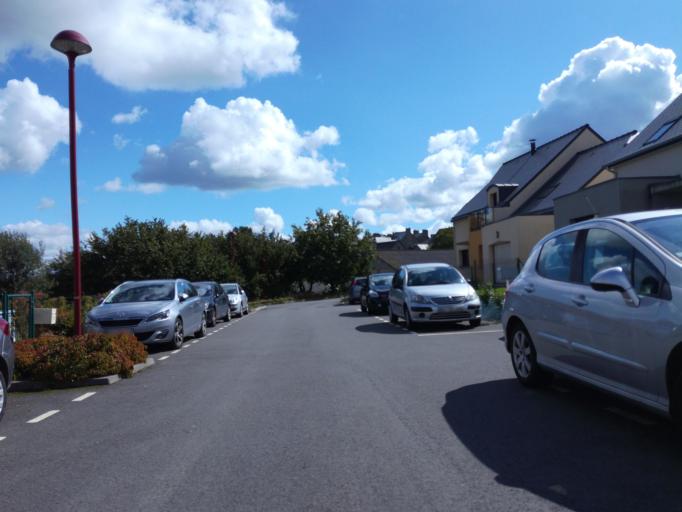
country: FR
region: Brittany
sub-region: Departement d'Ille-et-Vilaine
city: Saint-Aubin-du-Cormier
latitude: 48.2628
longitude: -1.4038
